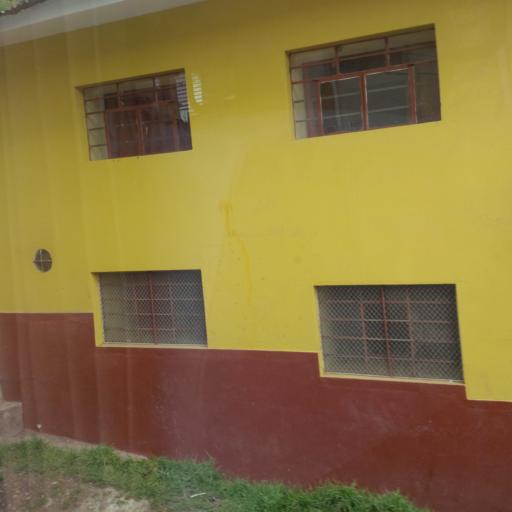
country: PE
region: Cusco
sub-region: Provincia de Cusco
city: Cusco
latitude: -13.5134
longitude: -71.9809
